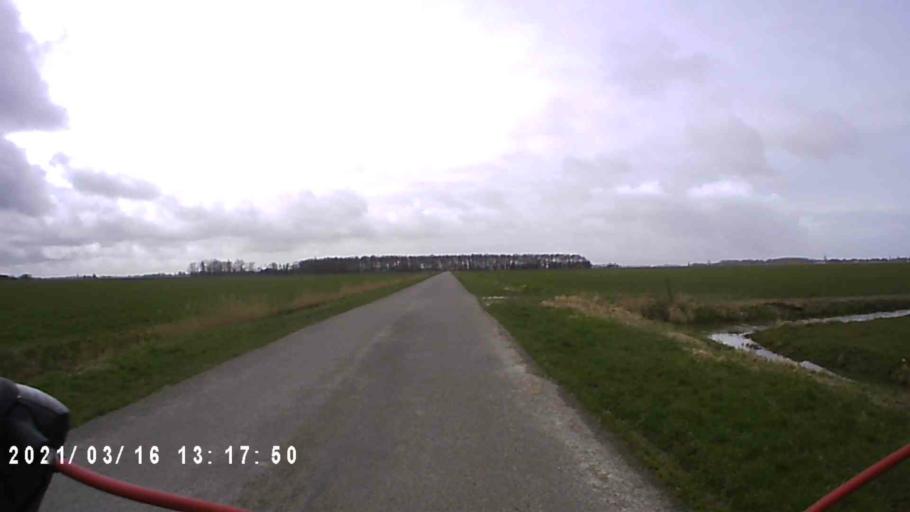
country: NL
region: Friesland
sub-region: Gemeente Het Bildt
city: Minnertsga
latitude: 53.2361
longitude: 5.5886
